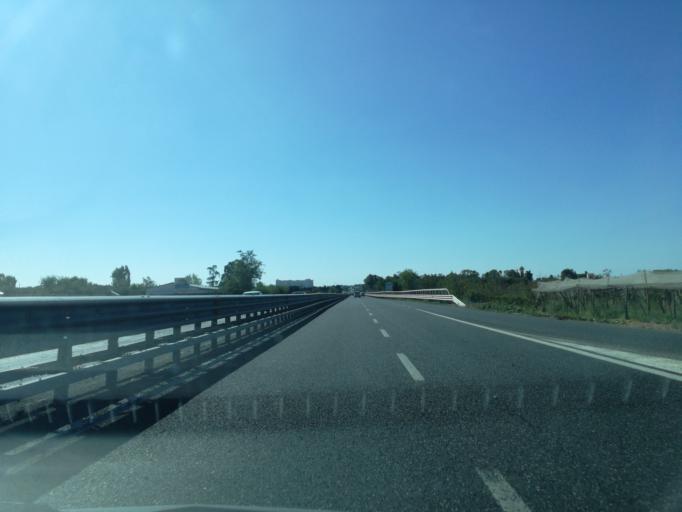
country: IT
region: Apulia
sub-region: Provincia di Bari
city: Cellamare
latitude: 40.9999
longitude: 16.9133
